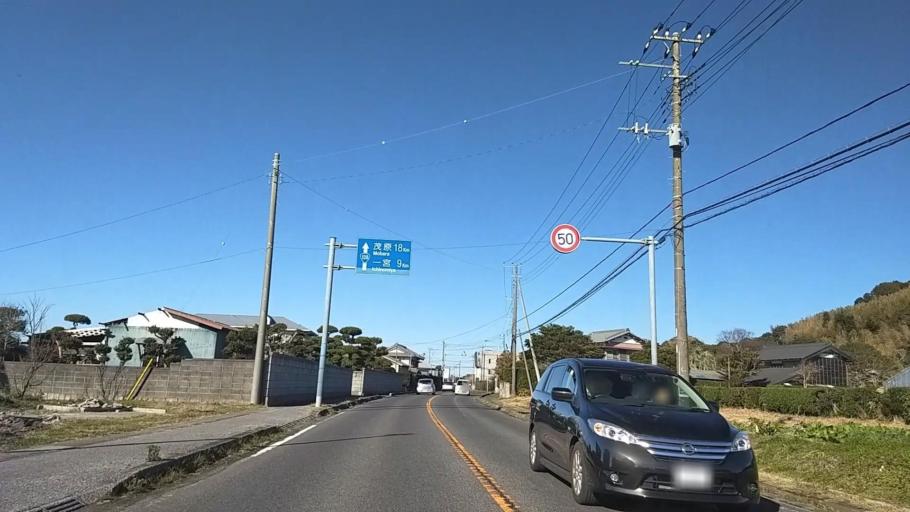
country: JP
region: Chiba
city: Ohara
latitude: 35.3125
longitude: 140.4025
